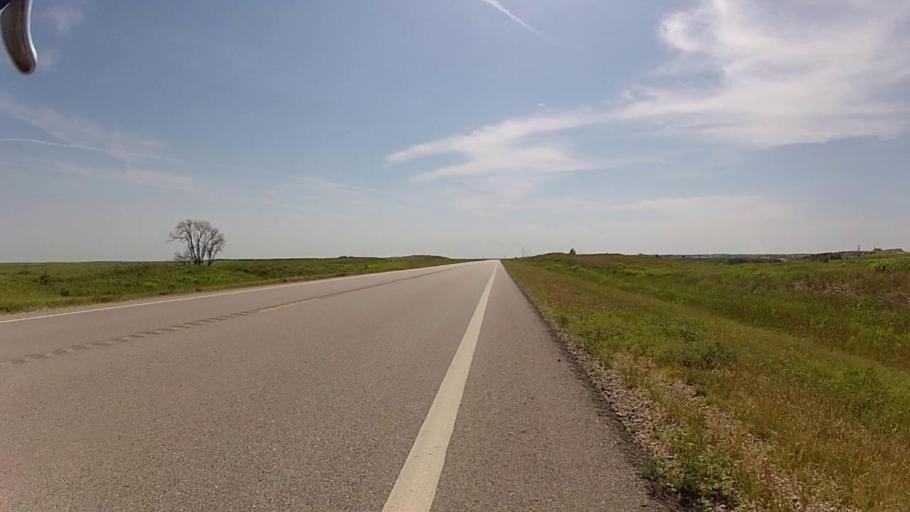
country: US
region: Kansas
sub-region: Cowley County
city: Winfield
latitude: 37.1110
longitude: -96.6123
